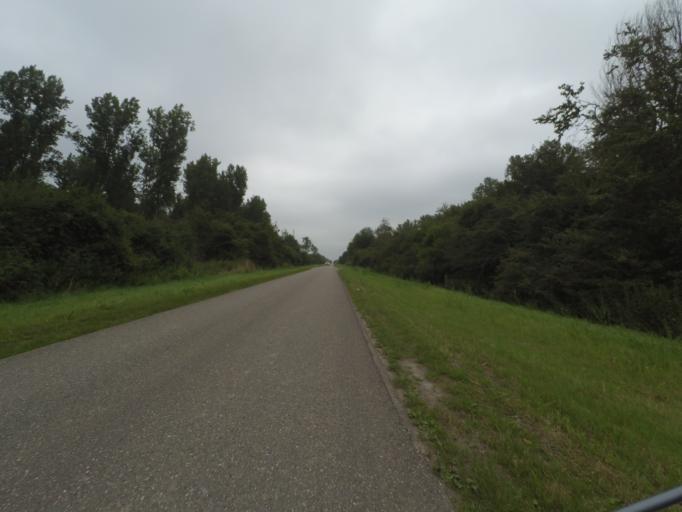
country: NL
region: Flevoland
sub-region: Gemeente Lelystad
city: Lelystad
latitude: 52.4633
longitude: 5.4395
